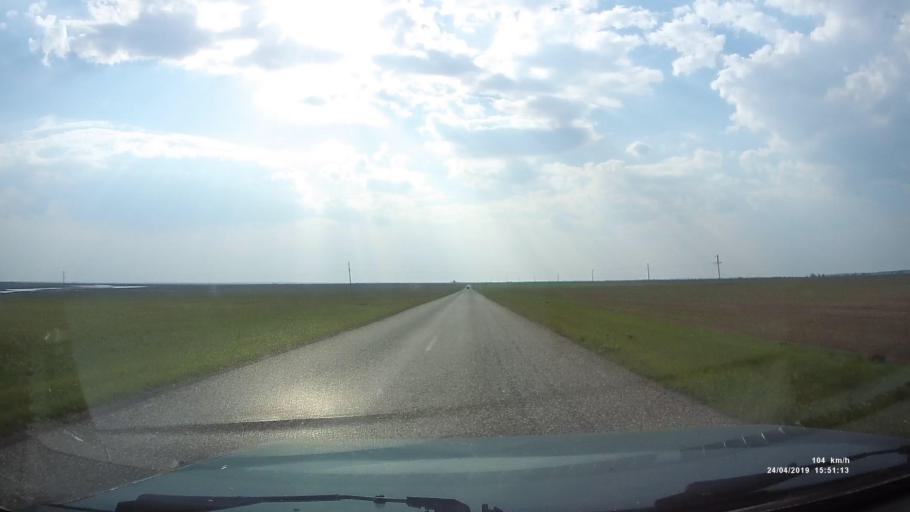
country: RU
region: Kalmykiya
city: Yashalta
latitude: 46.6043
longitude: 42.6156
